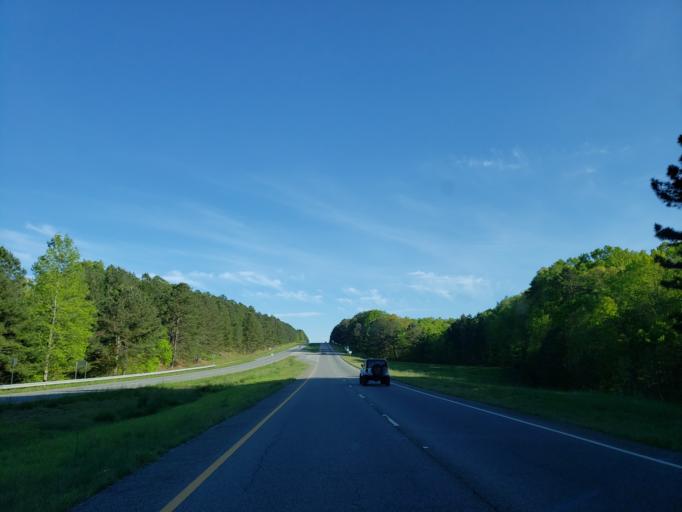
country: US
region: Georgia
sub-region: Polk County
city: Rockmart
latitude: 33.9544
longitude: -84.9840
